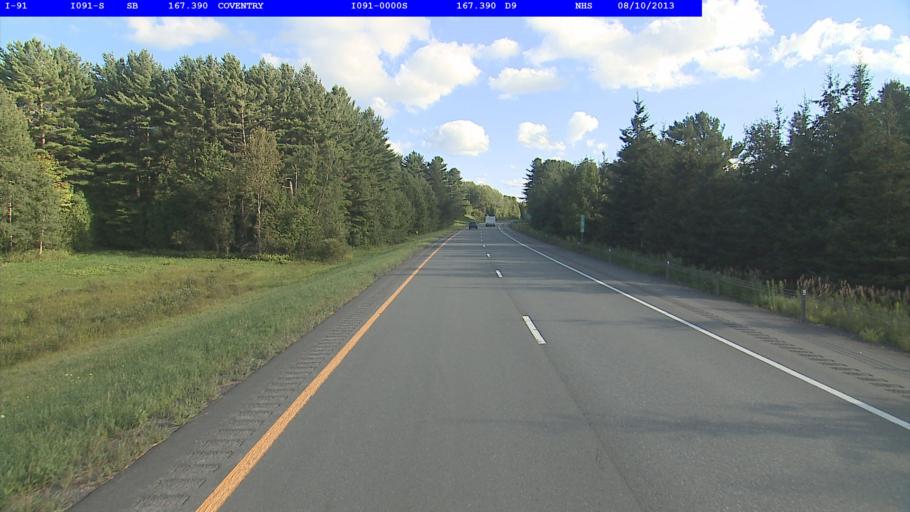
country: US
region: Vermont
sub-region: Orleans County
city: Newport
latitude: 44.8854
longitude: -72.1722
